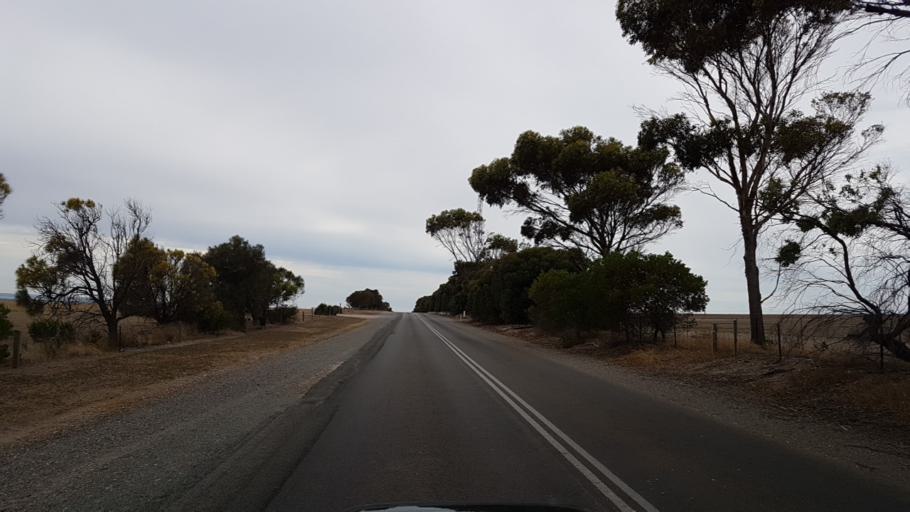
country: AU
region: South Australia
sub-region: Yorke Peninsula
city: Honiton
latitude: -34.9850
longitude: 137.2625
